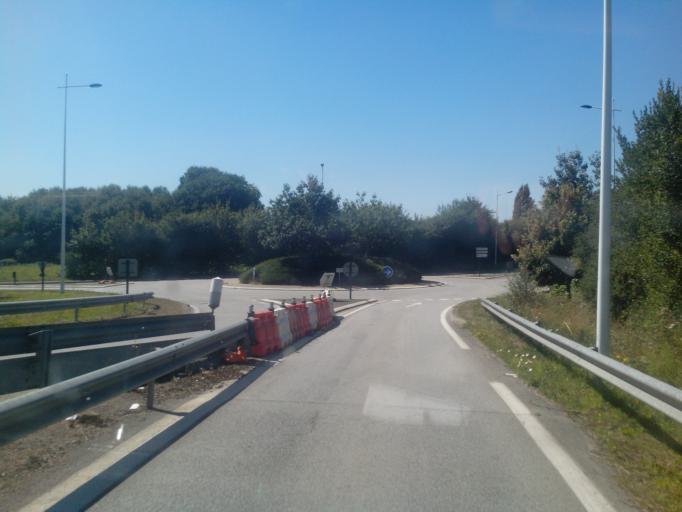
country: FR
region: Brittany
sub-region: Departement des Cotes-d'Armor
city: Loudeac
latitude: 48.1693
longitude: -2.7353
